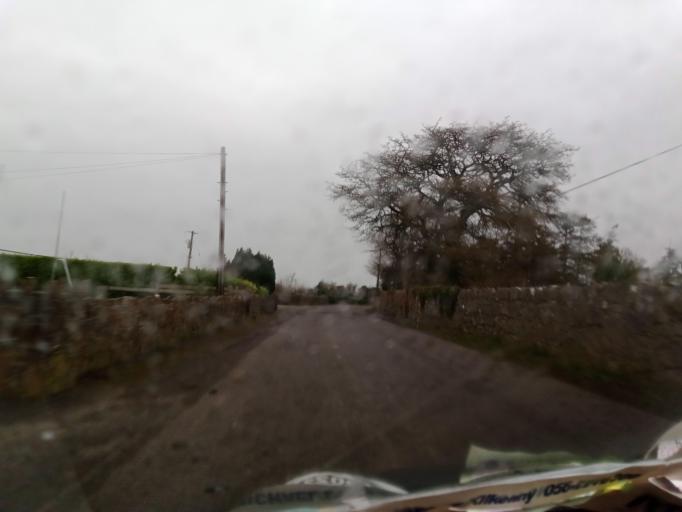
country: IE
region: Munster
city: Fethard
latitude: 52.5599
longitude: -7.7663
